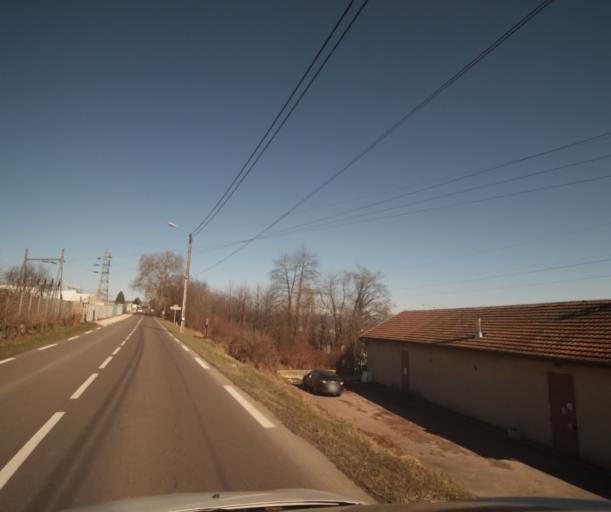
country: FR
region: Franche-Comte
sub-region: Departement du Doubs
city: Thise
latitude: 47.2677
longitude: 6.0535
